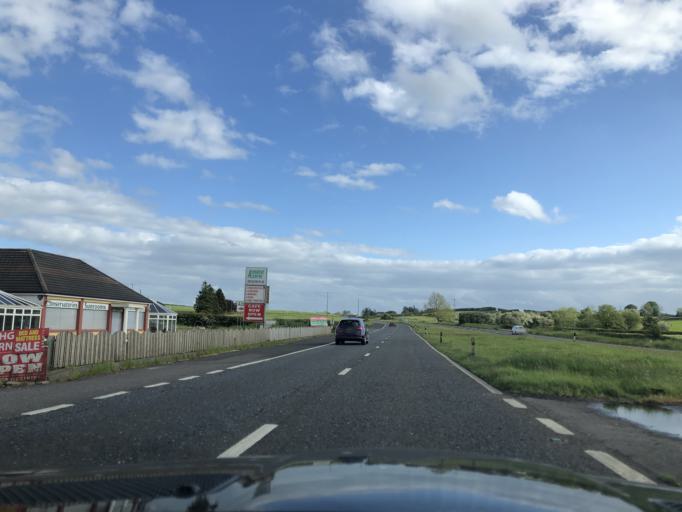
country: GB
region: Northern Ireland
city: Cullybackey
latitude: 54.9331
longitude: -6.3275
